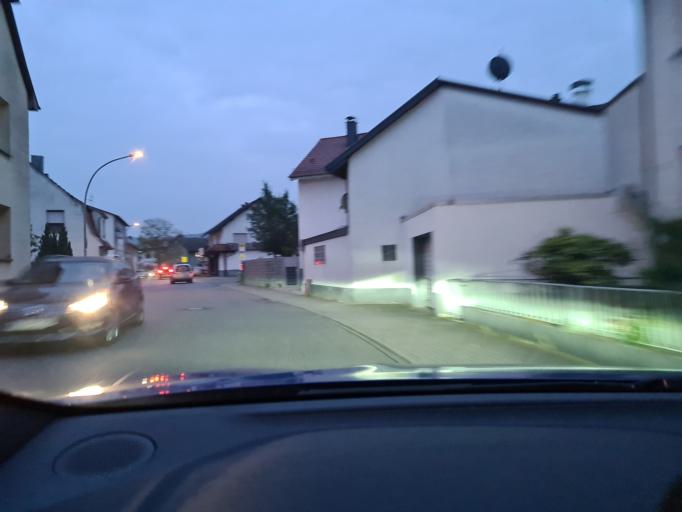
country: DE
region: Baden-Wuerttemberg
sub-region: Karlsruhe Region
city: Dielheim
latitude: 49.2836
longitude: 8.7326
